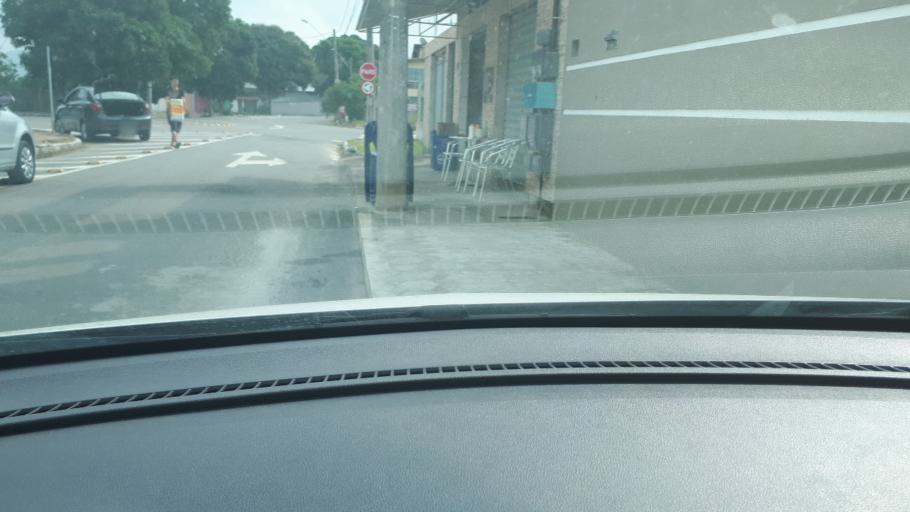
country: BR
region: Espirito Santo
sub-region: Serra
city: Serra
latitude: -20.1475
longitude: -40.1978
